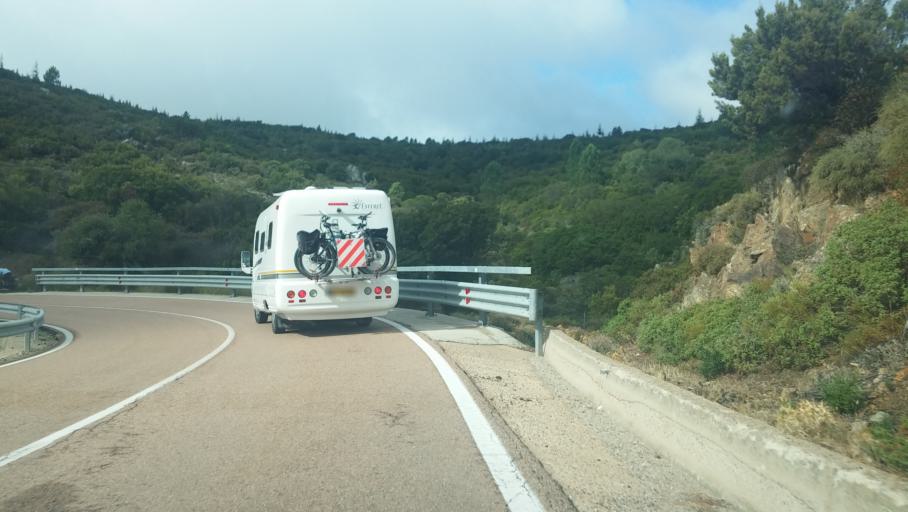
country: IT
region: Sardinia
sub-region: Provincia di Ogliastra
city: Urzulei
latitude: 40.1703
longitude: 9.5261
